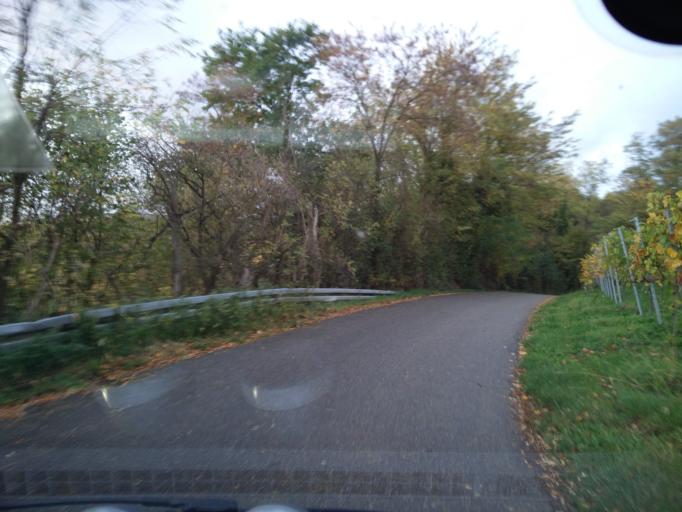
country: DE
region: Baden-Wuerttemberg
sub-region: Freiburg Region
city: Fischingen
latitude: 47.6544
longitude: 7.6119
